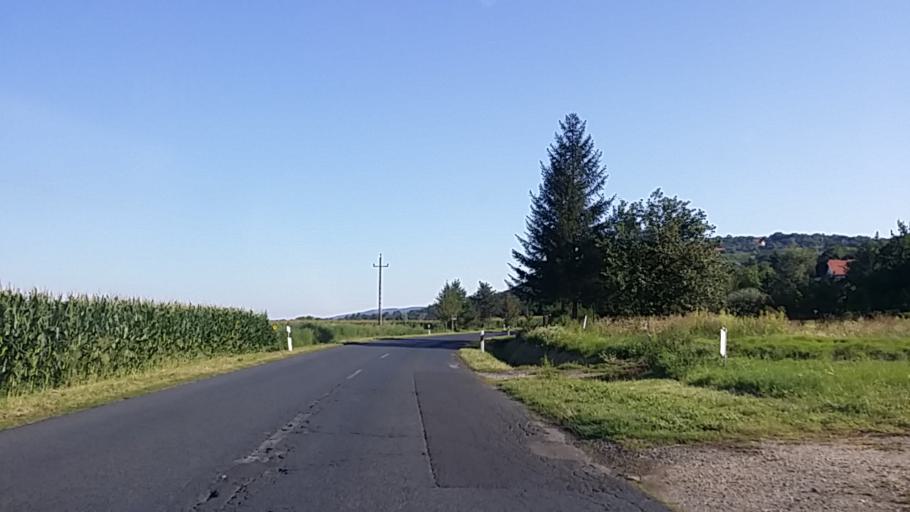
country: HU
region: Zala
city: Cserszegtomaj
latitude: 46.8169
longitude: 17.2022
